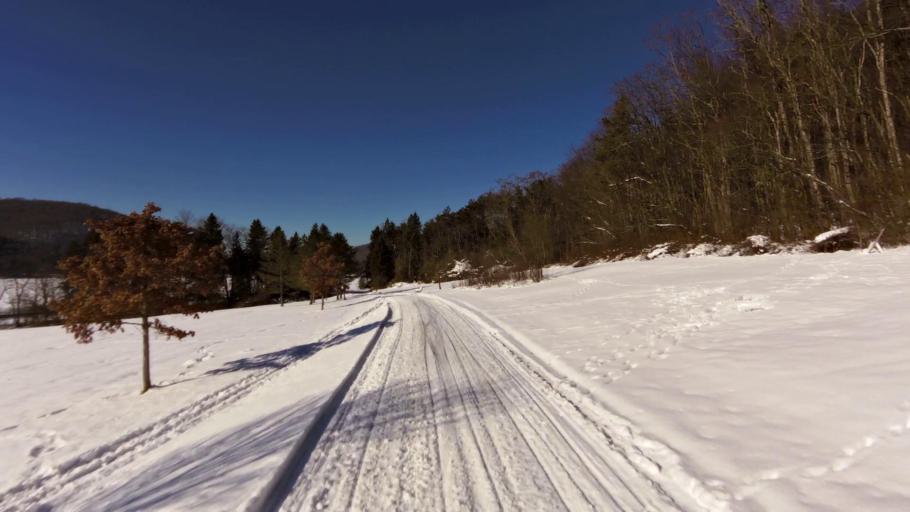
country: US
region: New York
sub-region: Cattaraugus County
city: Salamanca
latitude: 42.1038
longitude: -78.7395
